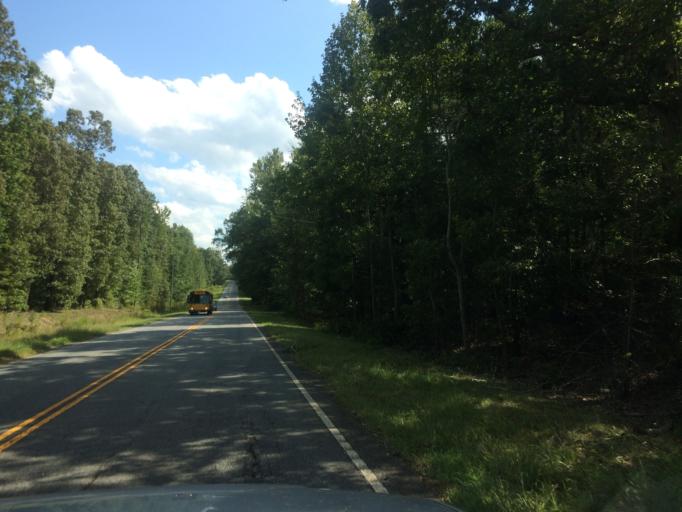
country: US
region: South Carolina
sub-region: Anderson County
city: Belton
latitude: 34.4860
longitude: -82.4543
